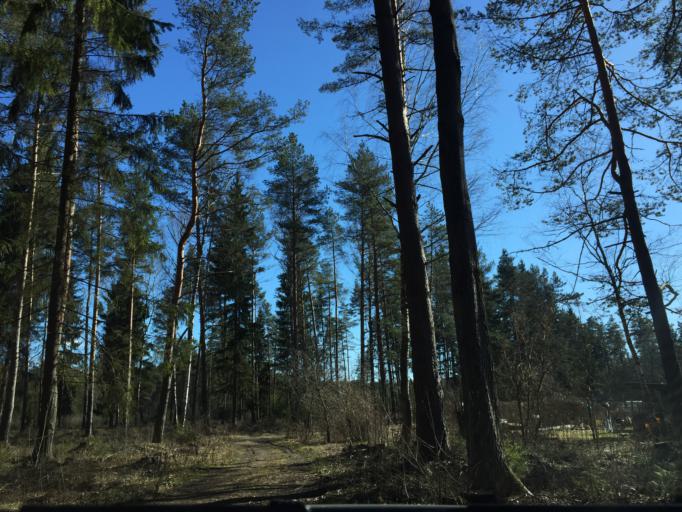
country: LV
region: Incukalns
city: Vangazi
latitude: 57.0908
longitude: 24.5371
